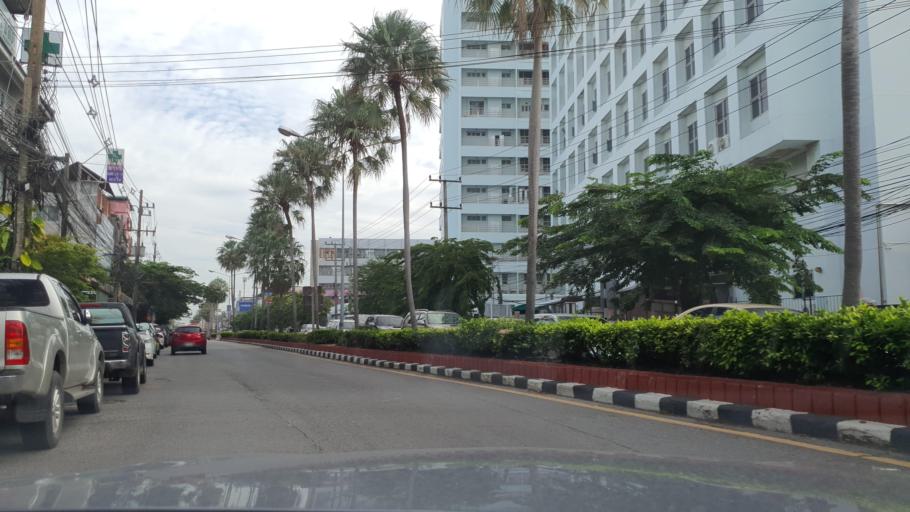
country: TH
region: Rayong
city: Rayong
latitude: 12.6820
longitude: 101.2760
